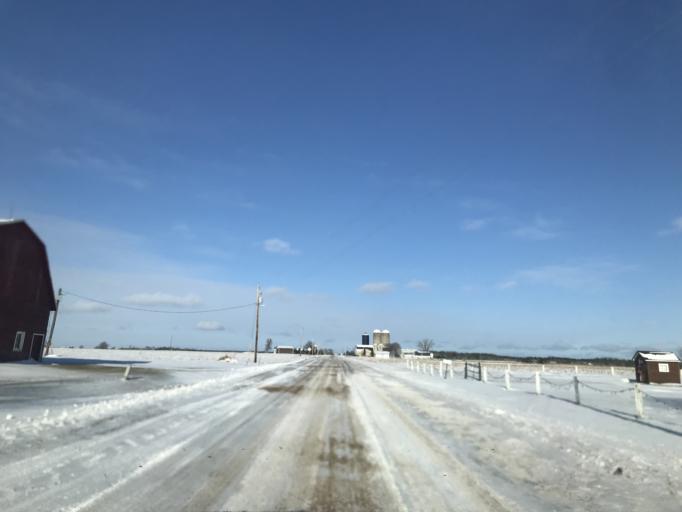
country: US
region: Wisconsin
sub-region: Kewaunee County
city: Algoma
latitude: 44.6978
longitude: -87.6003
